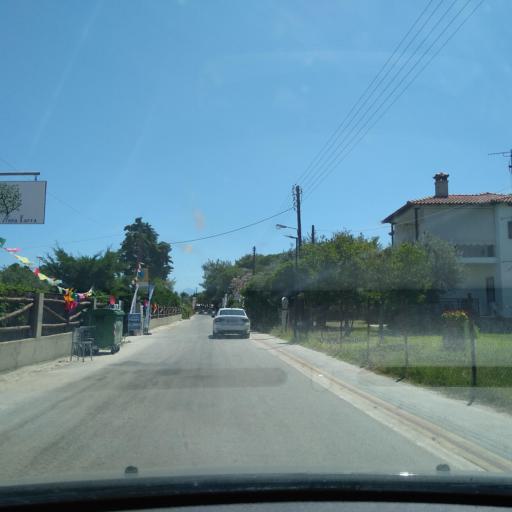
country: GR
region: Central Macedonia
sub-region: Nomos Chalkidikis
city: Neos Marmaras
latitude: 40.1871
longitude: 23.7888
